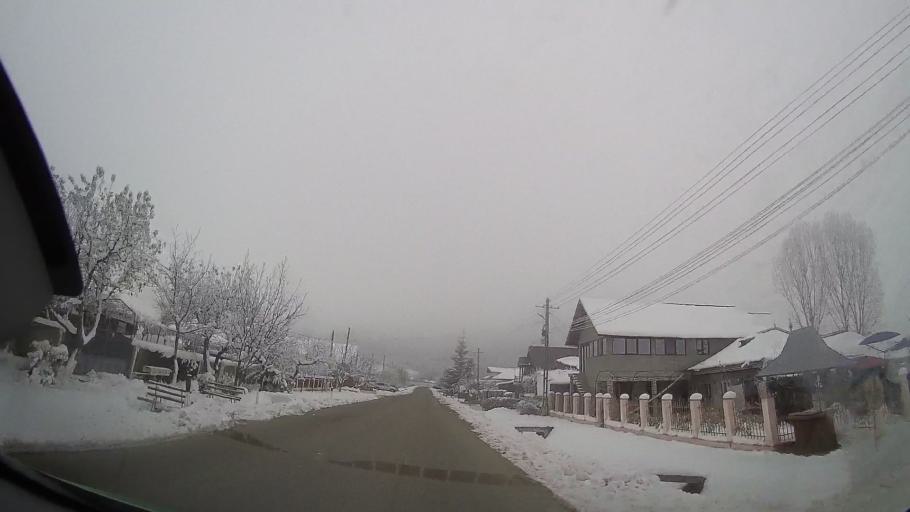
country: RO
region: Neamt
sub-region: Comuna Valea Ursului
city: Valea Ursului
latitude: 46.8506
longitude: 27.0489
